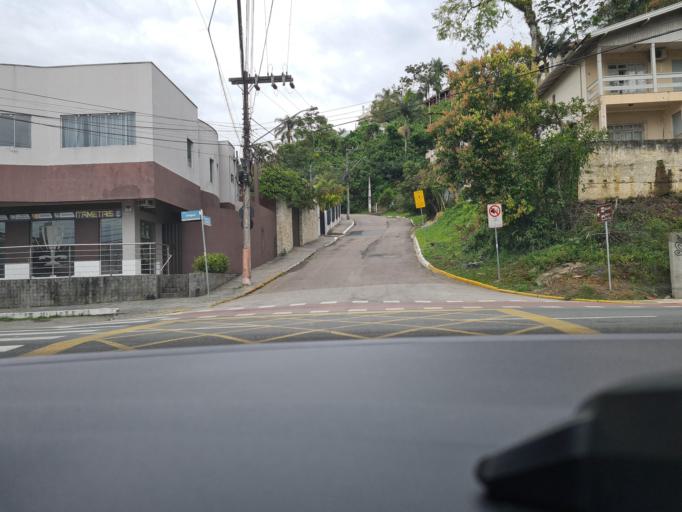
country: BR
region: Santa Catarina
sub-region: Itajai
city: Itajai
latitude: -26.9170
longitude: -48.6583
